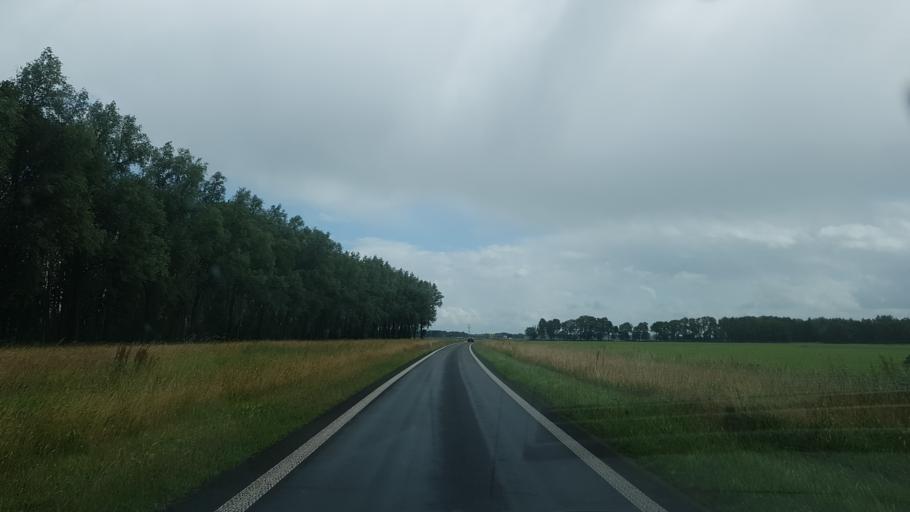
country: NL
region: Friesland
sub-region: Gemeente Dantumadiel
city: Rinsumageast
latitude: 53.3009
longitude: 5.9470
